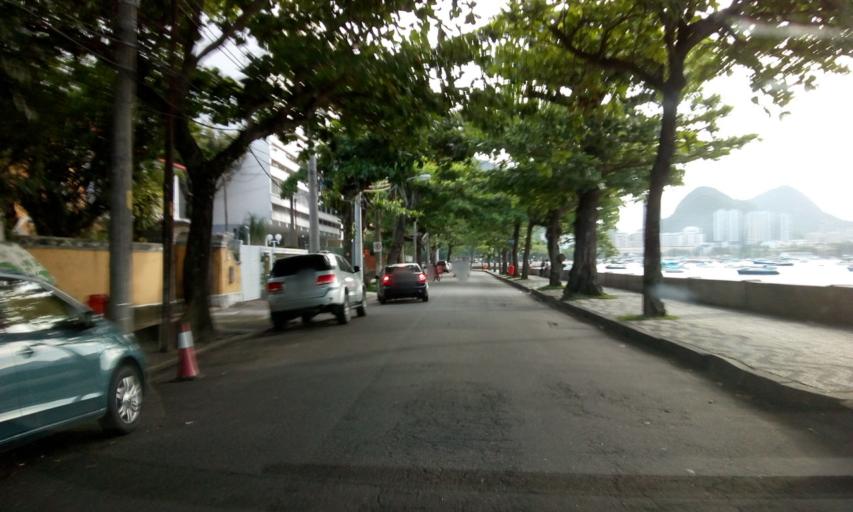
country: BR
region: Rio de Janeiro
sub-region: Rio De Janeiro
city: Rio de Janeiro
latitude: -22.9447
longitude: -43.1629
